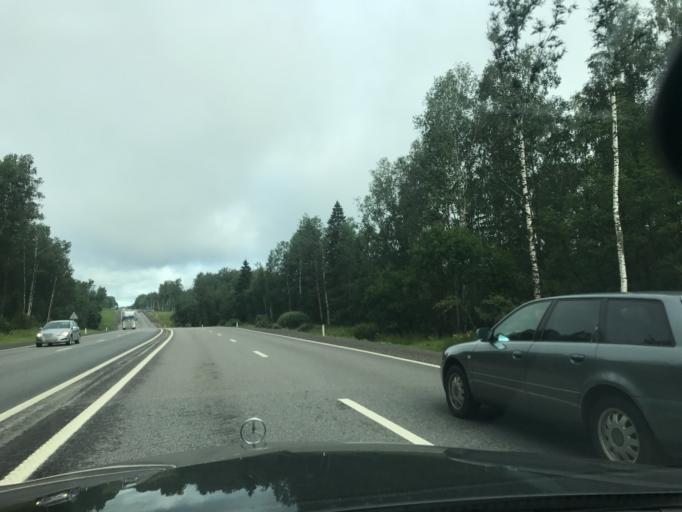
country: RU
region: Smolensk
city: Gagarin
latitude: 55.4986
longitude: 35.2506
